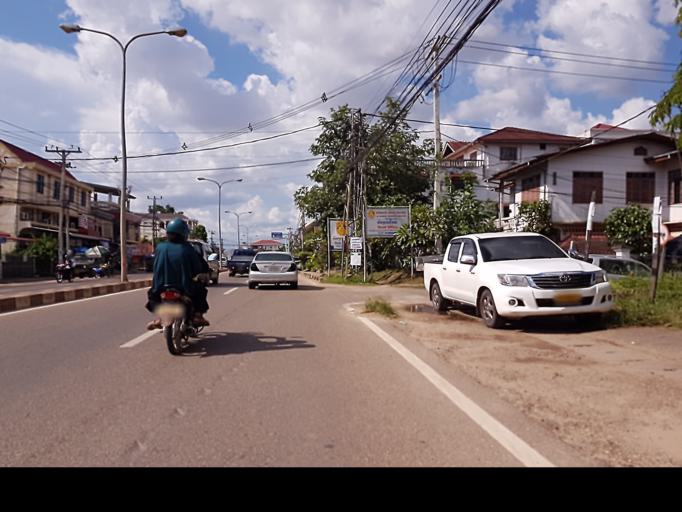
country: TH
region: Nong Khai
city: Si Chiang Mai
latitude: 17.9173
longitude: 102.6197
